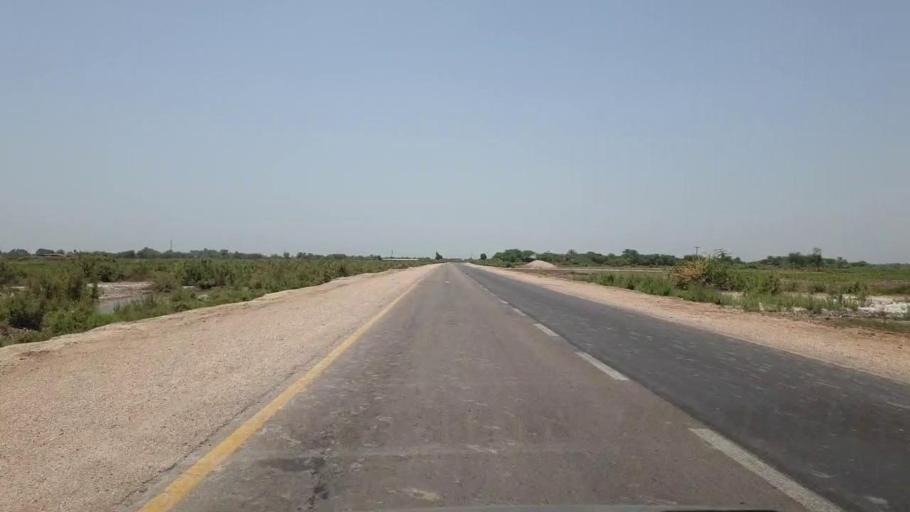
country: PK
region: Sindh
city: Sakrand
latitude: 26.1260
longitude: 68.3804
